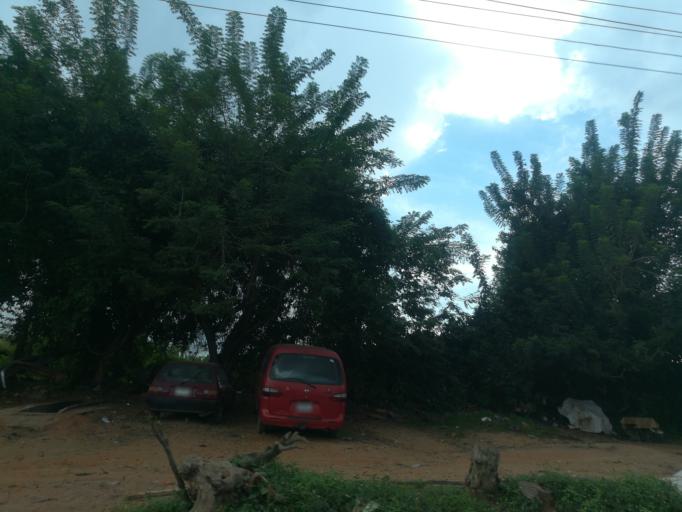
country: NG
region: Oyo
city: Ibadan
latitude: 7.4311
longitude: 3.8953
